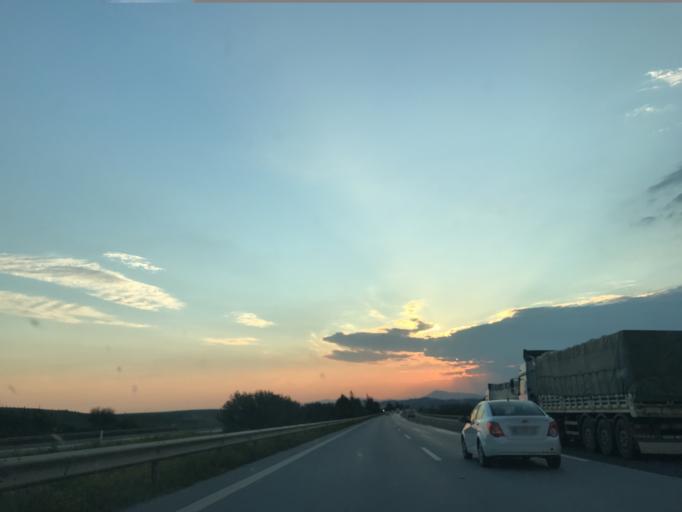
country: TR
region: Mersin
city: Yenice
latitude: 37.0139
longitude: 34.9958
